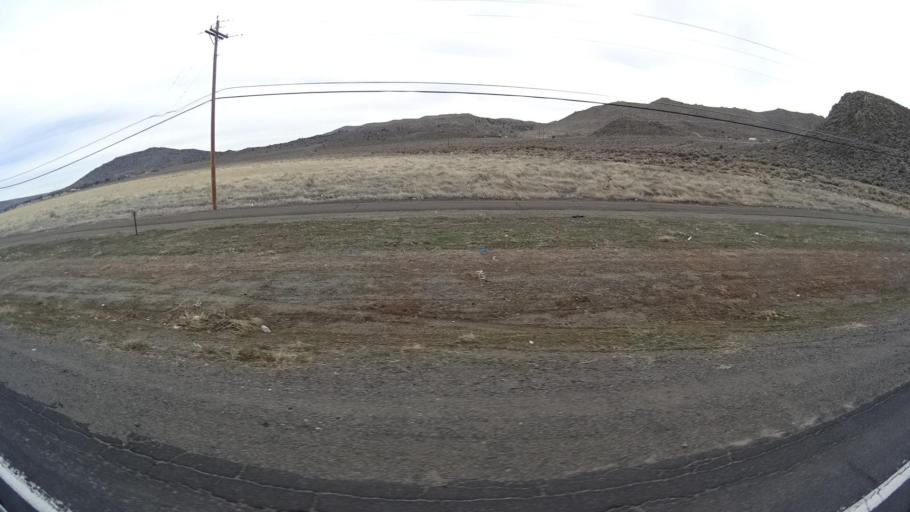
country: US
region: Nevada
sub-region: Washoe County
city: Lemmon Valley
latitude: 39.6501
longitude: -119.8285
